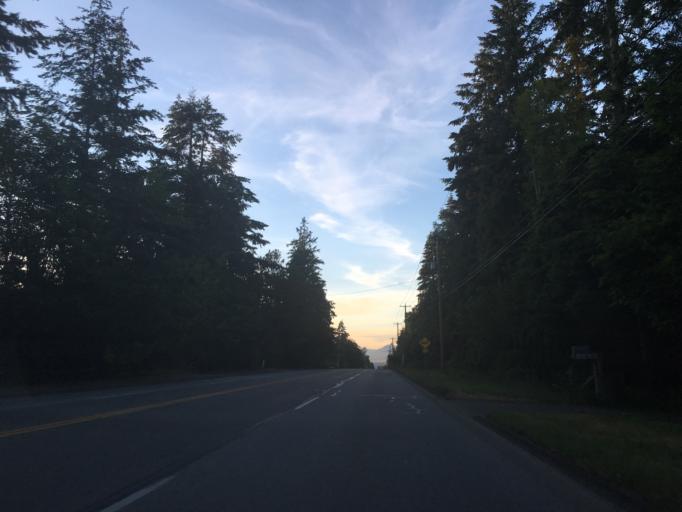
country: US
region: Washington
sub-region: Whatcom County
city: Blaine
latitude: 49.0410
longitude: -122.7351
